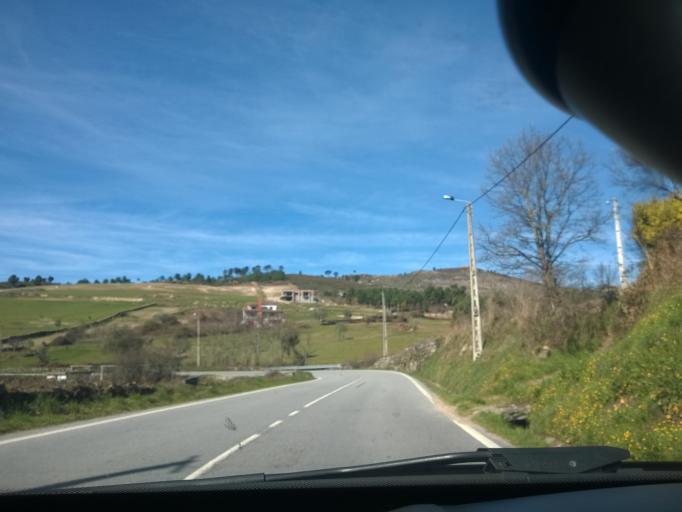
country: PT
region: Vila Real
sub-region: Chaves
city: Chaves
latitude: 41.7116
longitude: -7.5650
